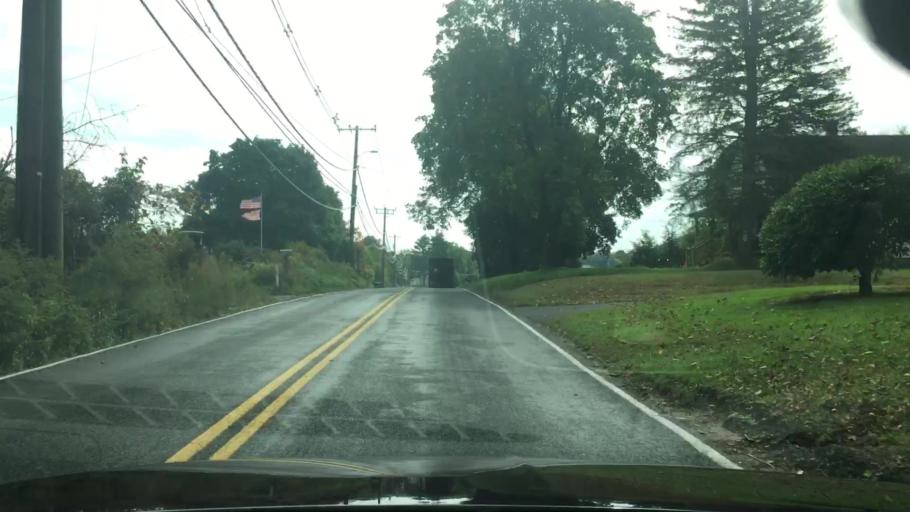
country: US
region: Connecticut
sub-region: Tolland County
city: Somers
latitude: 41.9803
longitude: -72.4876
